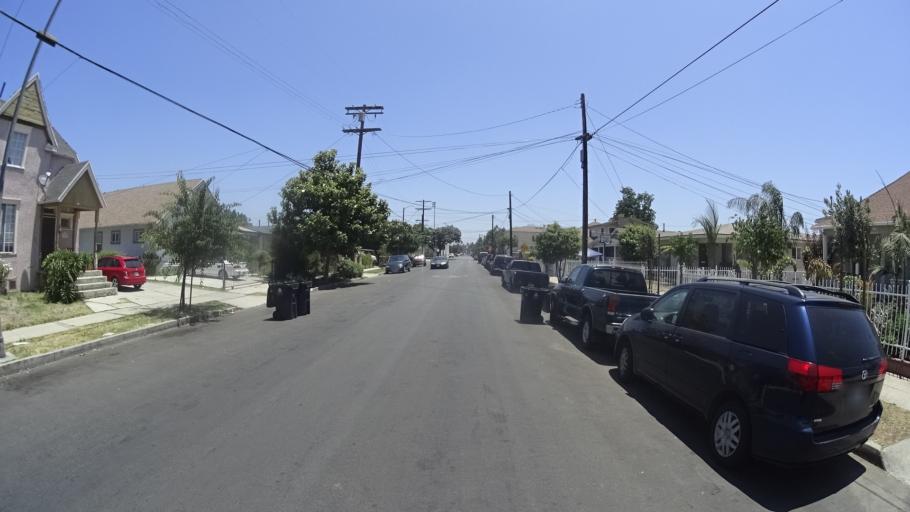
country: US
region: California
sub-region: Los Angeles County
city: View Park-Windsor Hills
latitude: 34.0228
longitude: -118.3059
